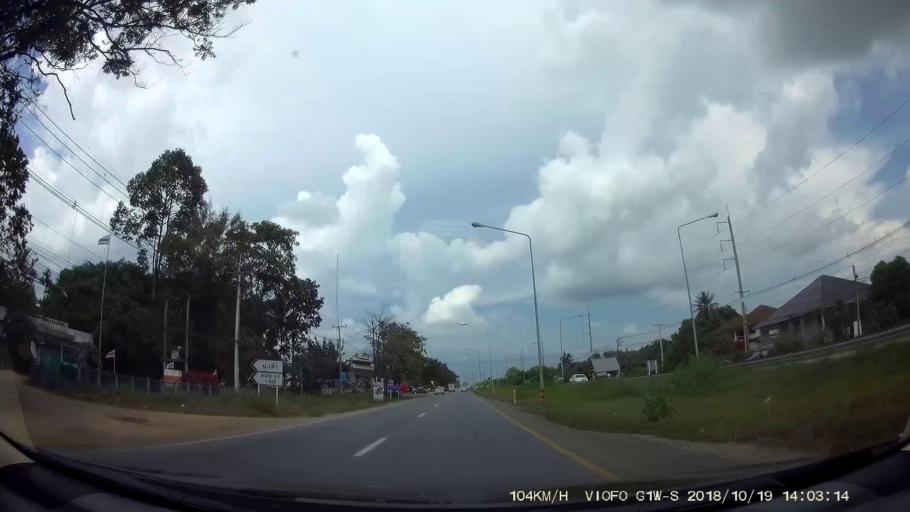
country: TH
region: Chaiyaphum
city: Chaiyaphum
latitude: 15.8503
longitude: 102.0684
